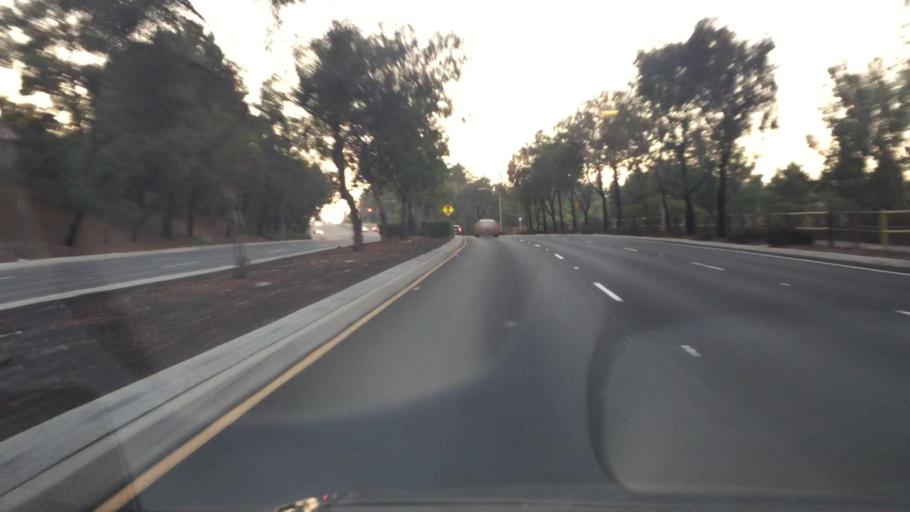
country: US
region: California
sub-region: San Diego County
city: Poway
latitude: 32.9859
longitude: -117.0646
